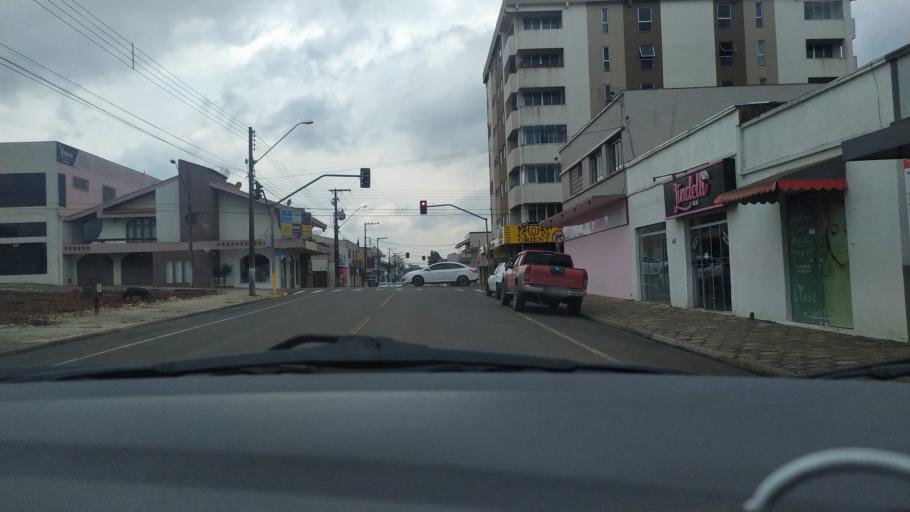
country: BR
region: Parana
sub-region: Palmas
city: Palmas
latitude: -26.4833
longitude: -51.9944
